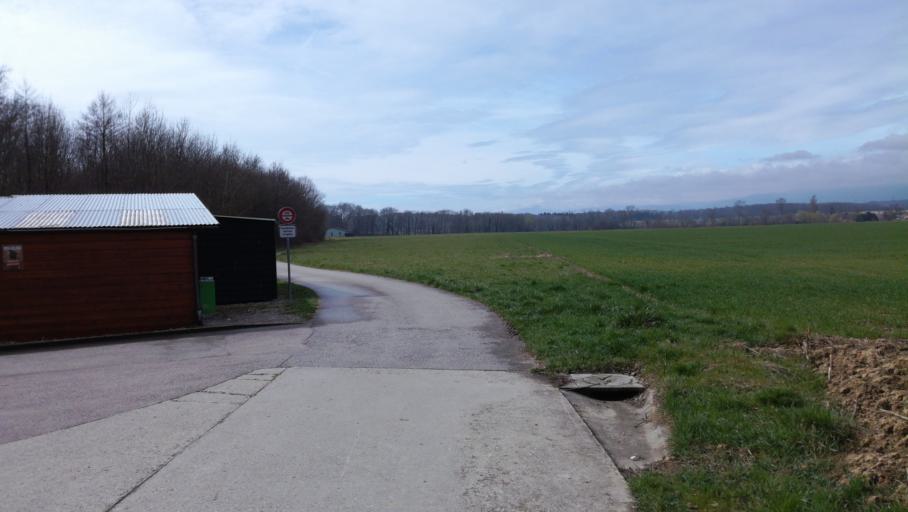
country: CH
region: Vaud
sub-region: Nyon District
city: Gland
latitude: 46.4405
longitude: 6.3006
